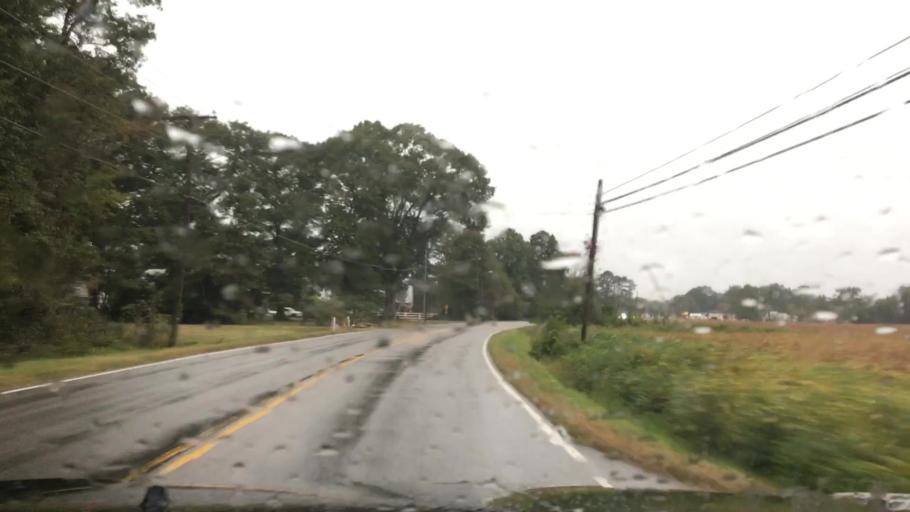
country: US
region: North Carolina
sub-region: Currituck County
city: Moyock
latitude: 36.6666
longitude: -76.2268
